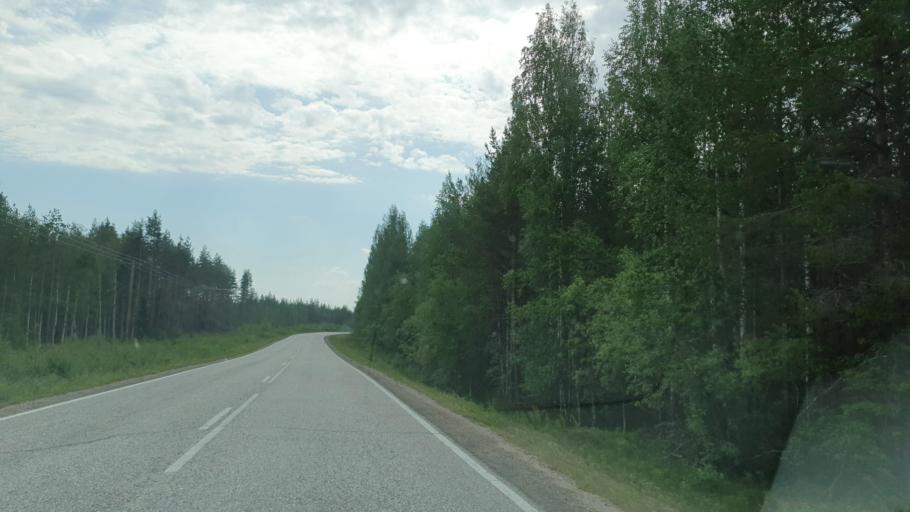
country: FI
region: Kainuu
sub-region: Kehys-Kainuu
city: Kuhmo
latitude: 64.2375
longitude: 29.8161
